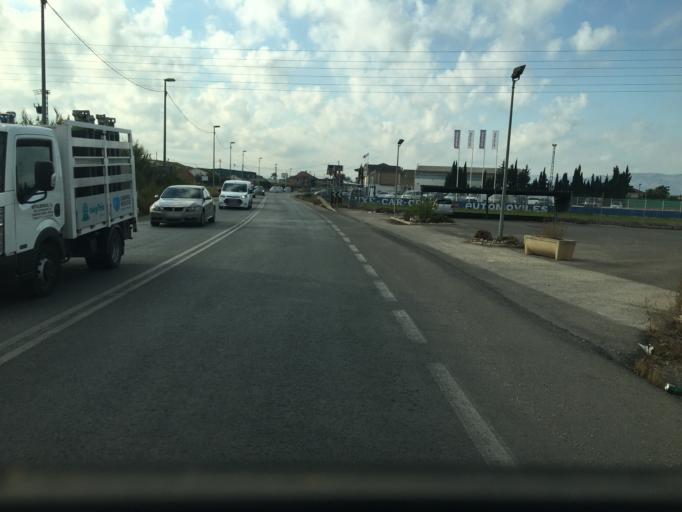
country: ES
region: Murcia
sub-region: Murcia
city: Santomera
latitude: 38.0393
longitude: -1.0476
